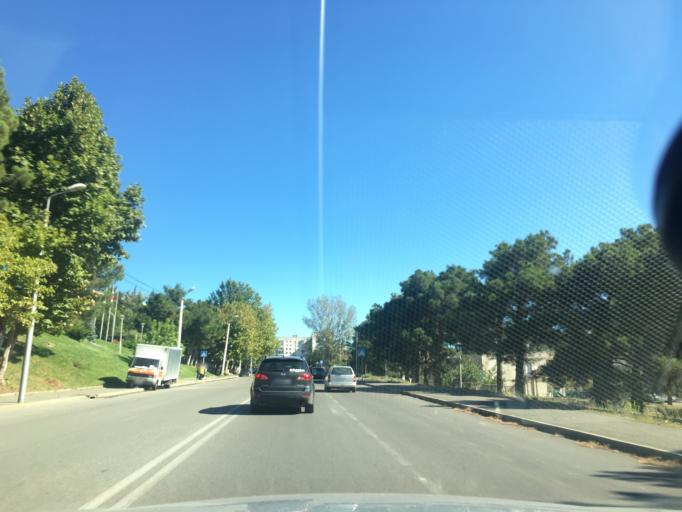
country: GE
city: Zahesi
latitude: 41.7973
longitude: 44.8110
